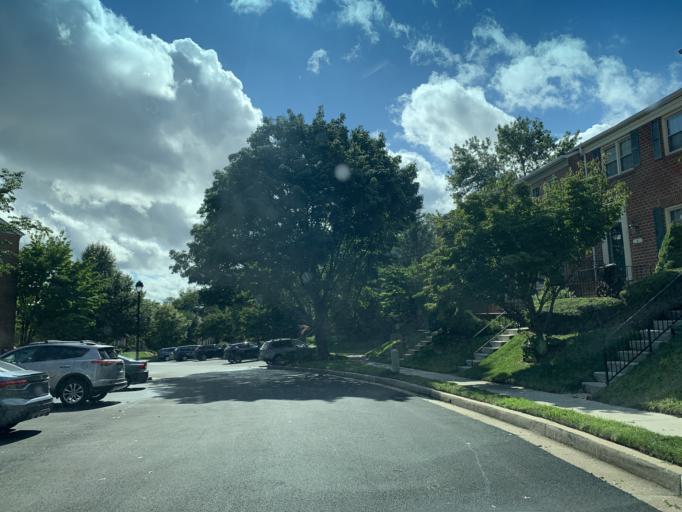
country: US
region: Maryland
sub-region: Baltimore County
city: Timonium
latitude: 39.4482
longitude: -76.6128
